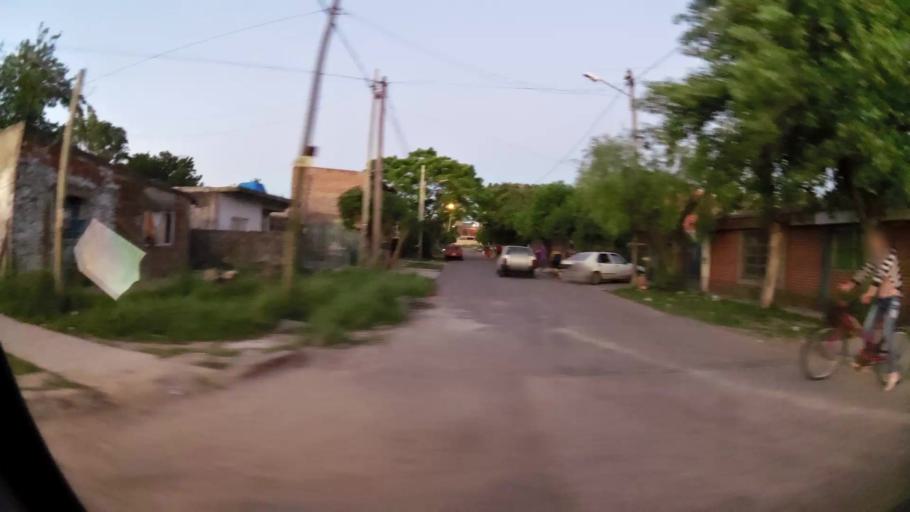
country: AR
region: Buenos Aires
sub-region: Partido de Quilmes
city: Quilmes
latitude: -34.7922
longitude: -58.1784
